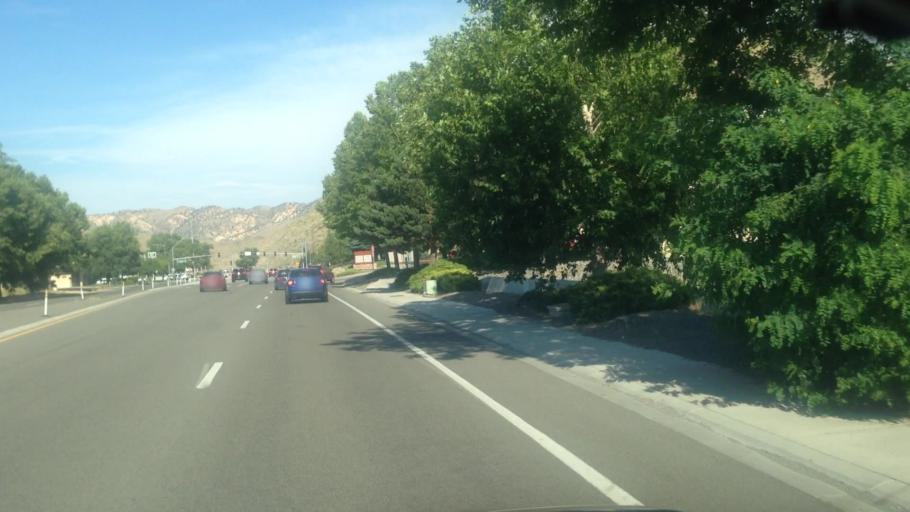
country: US
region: Nevada
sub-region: Washoe County
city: Sparks
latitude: 39.4768
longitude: -119.7681
